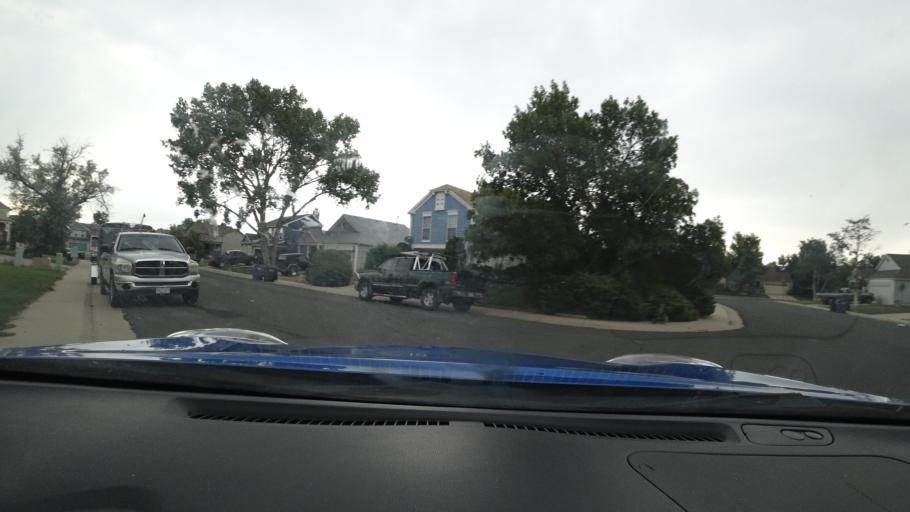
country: US
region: Colorado
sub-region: Adams County
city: Aurora
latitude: 39.7763
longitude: -104.7487
